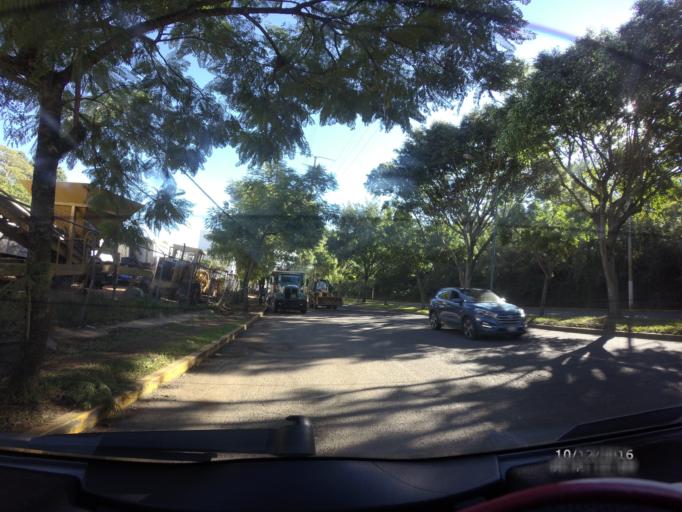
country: TR
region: Sivas
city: Karayun
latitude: 39.6695
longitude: 37.2921
